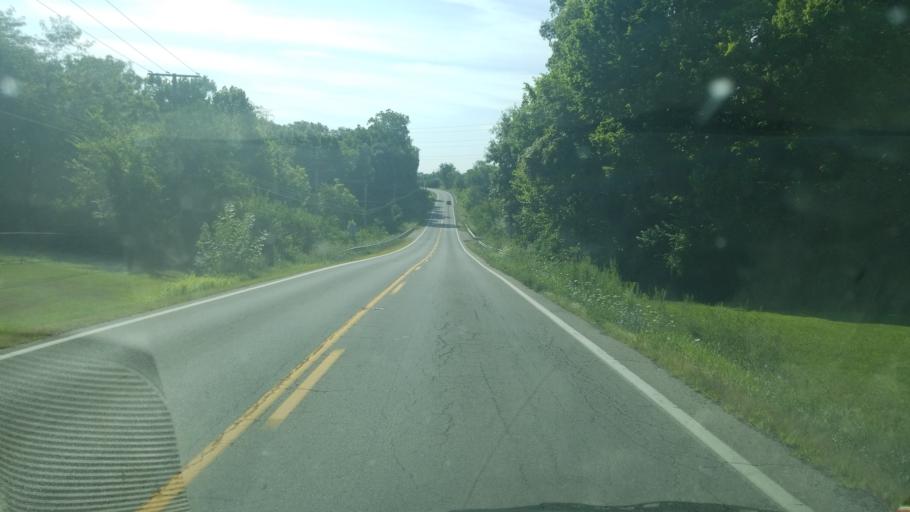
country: US
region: Ohio
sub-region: Franklin County
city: Grove City
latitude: 39.8486
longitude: -83.1585
